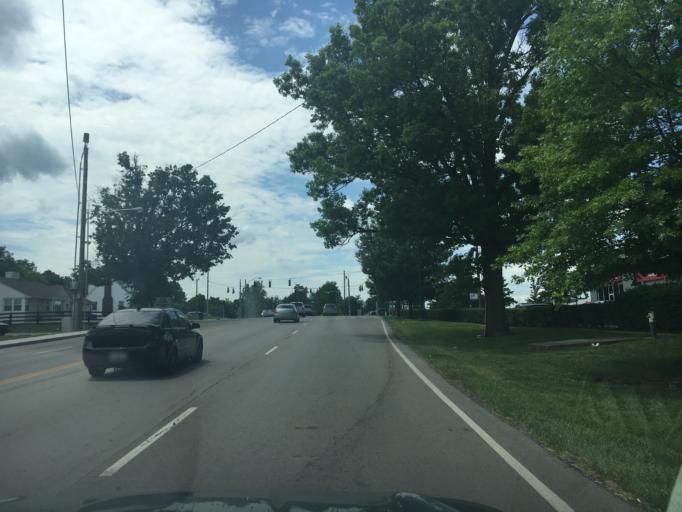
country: US
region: Kentucky
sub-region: Fayette County
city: Lexington-Fayette
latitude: 38.0648
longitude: -84.4772
